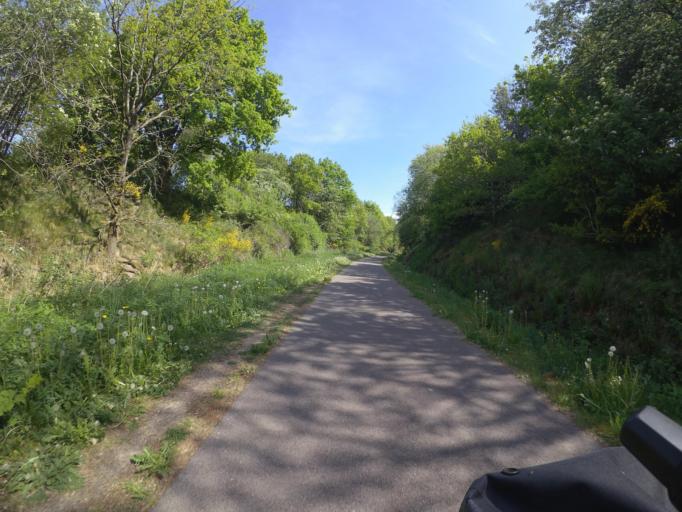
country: BE
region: Wallonia
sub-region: Province de Liege
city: Butgenbach
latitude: 50.4315
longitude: 6.1882
